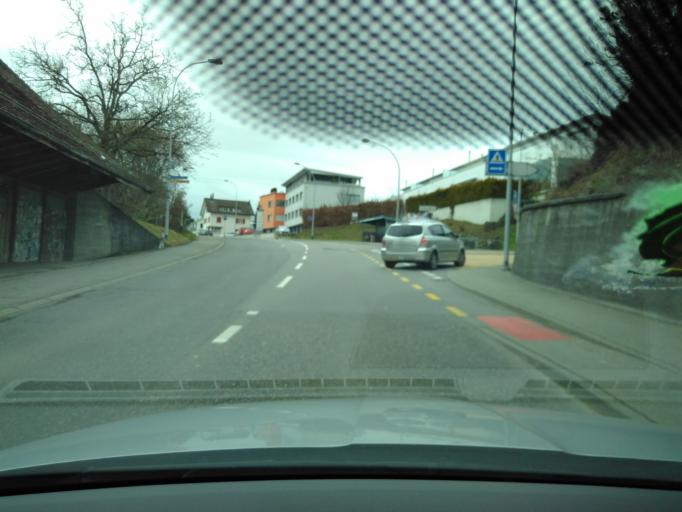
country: CH
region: Lucerne
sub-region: Hochdorf District
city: Emmen
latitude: 47.0971
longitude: 8.2716
